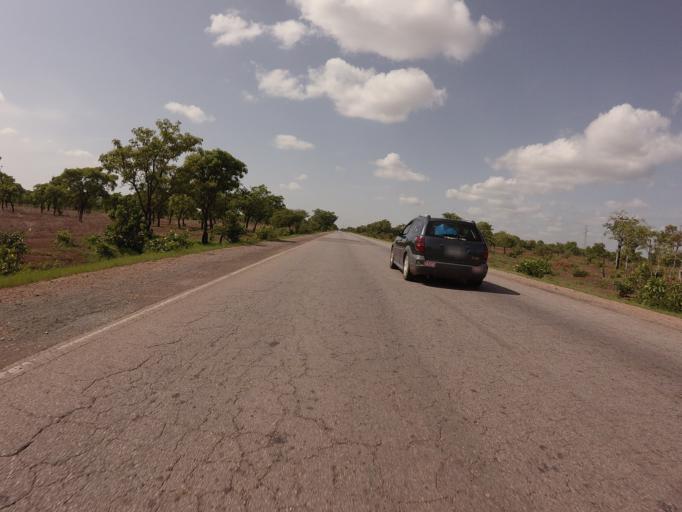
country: GH
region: Northern
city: Savelugu
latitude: 9.9588
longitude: -0.8334
